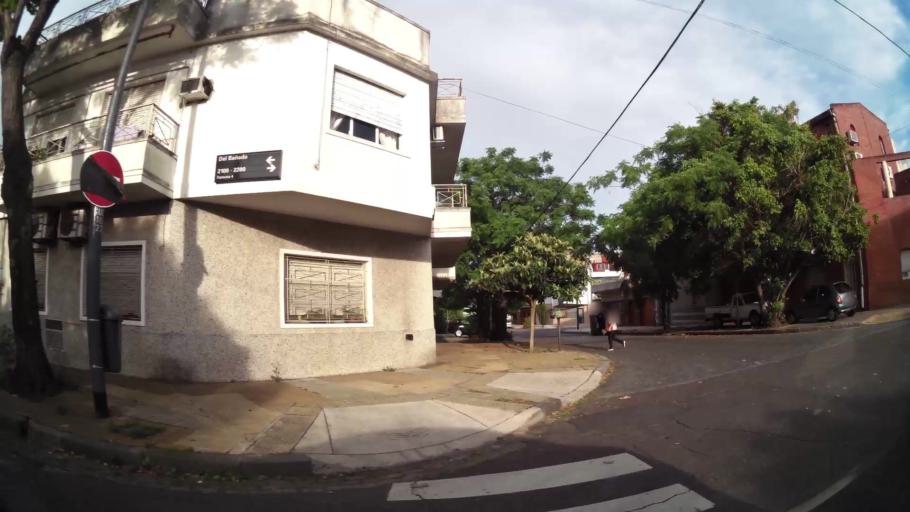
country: AR
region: Buenos Aires F.D.
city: Villa Lugano
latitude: -34.6422
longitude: -58.4282
